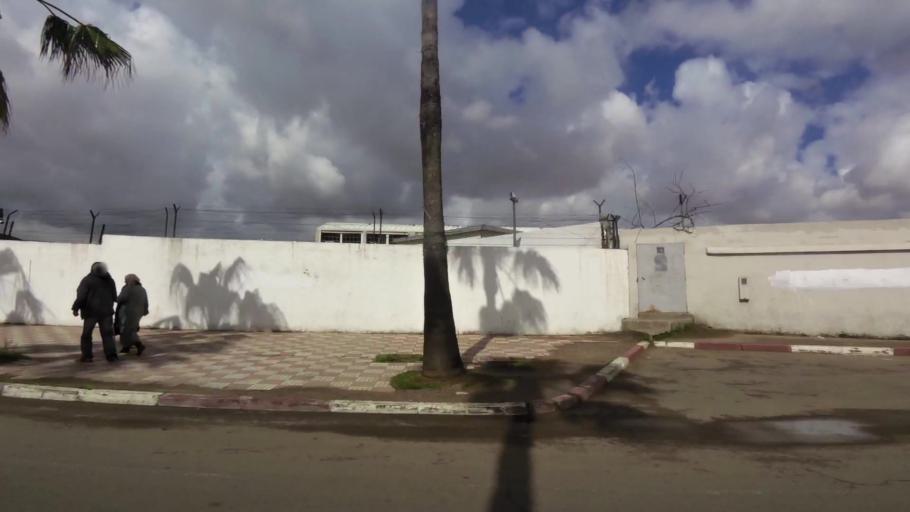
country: MA
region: Grand Casablanca
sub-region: Nouaceur
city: Bouskoura
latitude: 33.5246
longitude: -7.6514
